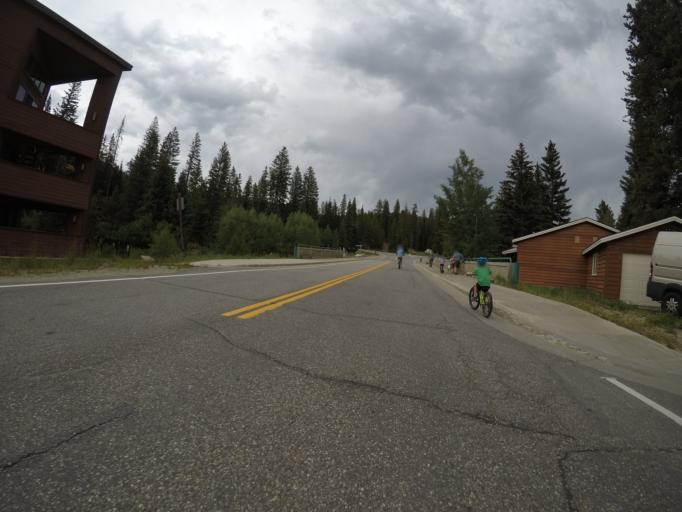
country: US
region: Colorado
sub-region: Grand County
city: Fraser
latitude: 39.8914
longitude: -105.7640
